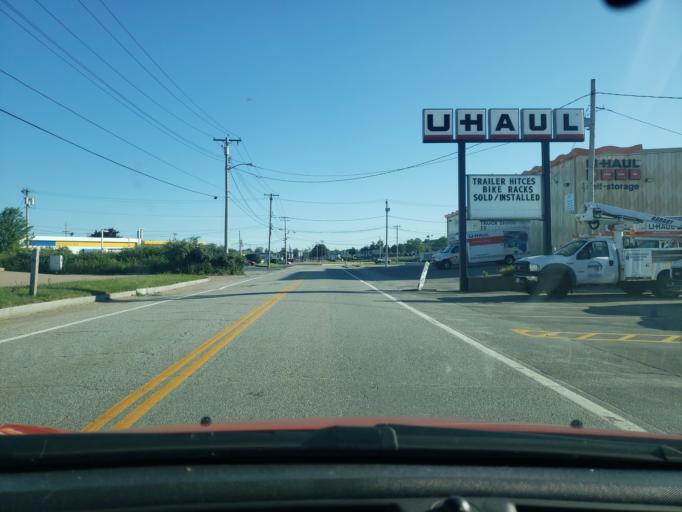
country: US
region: Rhode Island
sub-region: Newport County
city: Newport
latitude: 41.5052
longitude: -71.3176
